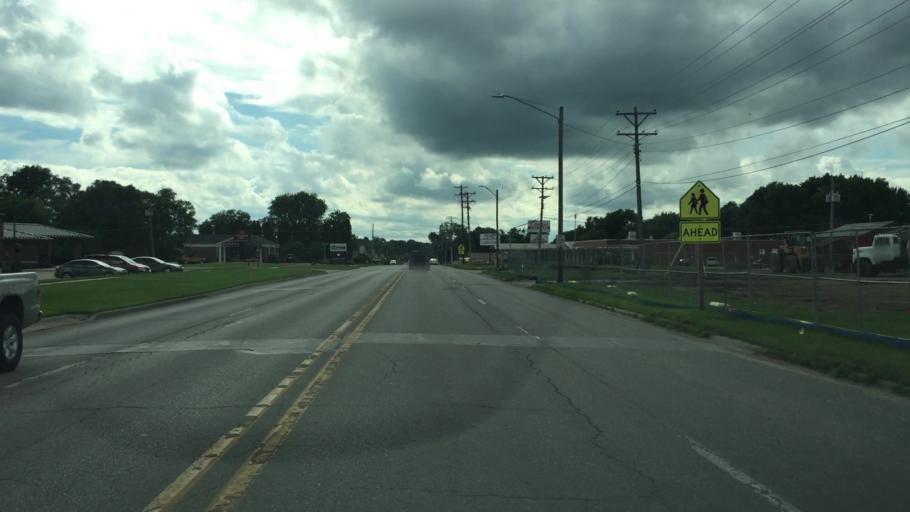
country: US
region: Iowa
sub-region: Jasper County
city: Newton
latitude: 41.6992
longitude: -93.0273
